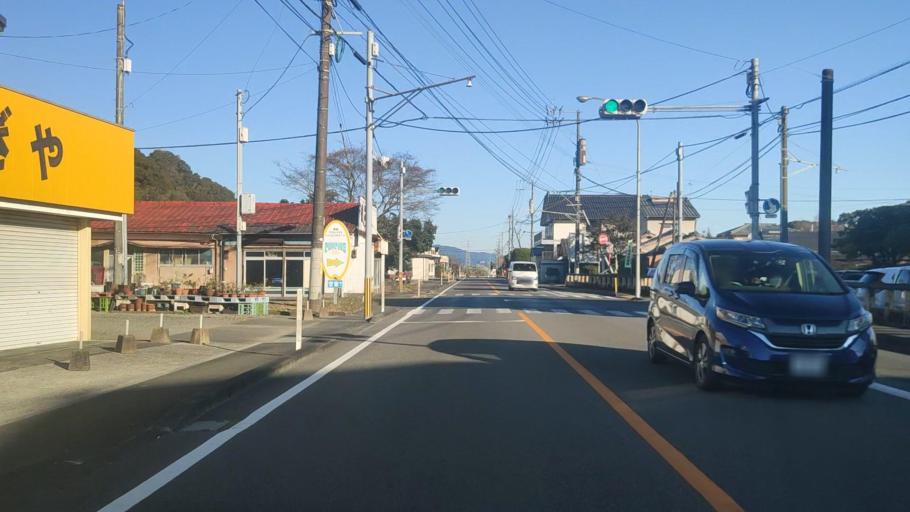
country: JP
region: Miyazaki
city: Nobeoka
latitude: 32.3851
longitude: 131.6275
